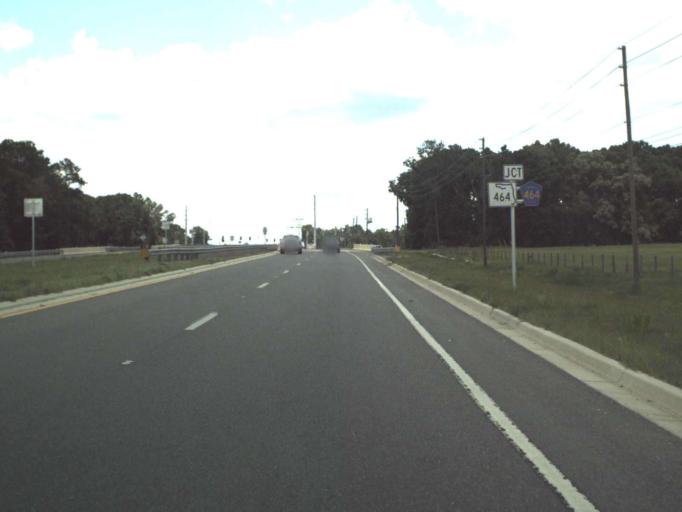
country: US
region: Florida
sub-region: Marion County
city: Silver Springs Shores
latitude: 29.1357
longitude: -82.0535
